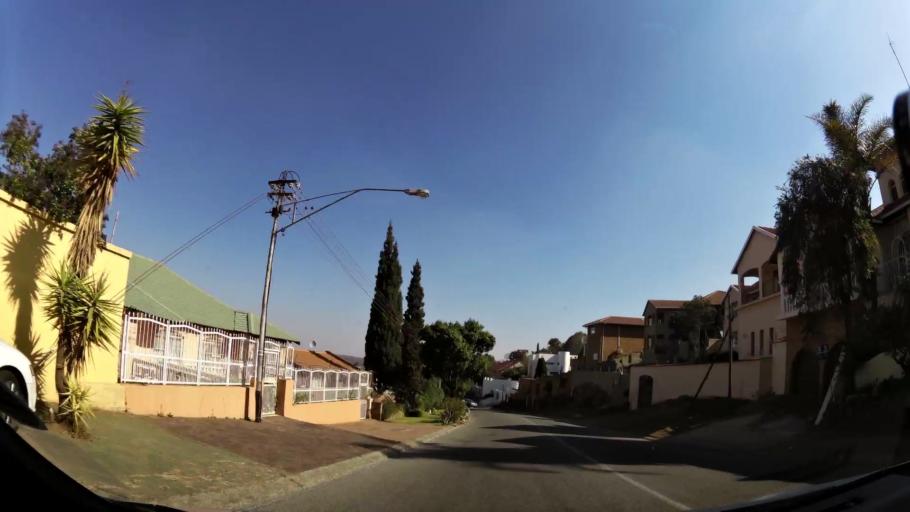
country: ZA
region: Gauteng
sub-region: City of Johannesburg Metropolitan Municipality
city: Johannesburg
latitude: -26.2618
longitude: 28.0527
